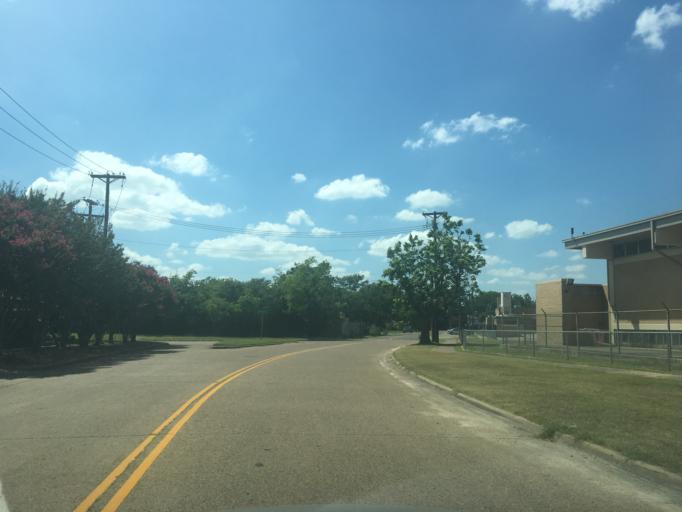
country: US
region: Texas
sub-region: Dallas County
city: Garland
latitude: 32.8359
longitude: -96.6909
